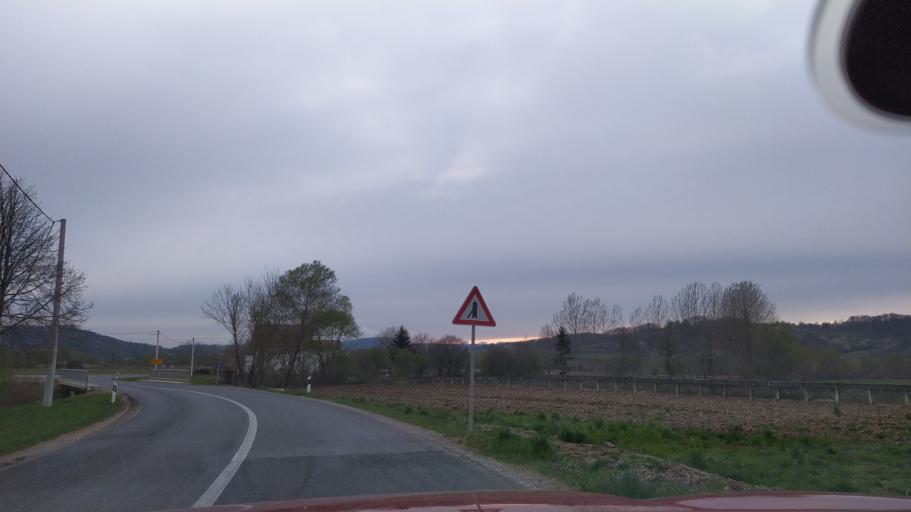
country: HR
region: Varazdinska
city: Jalzabet
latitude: 46.2115
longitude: 16.4712
